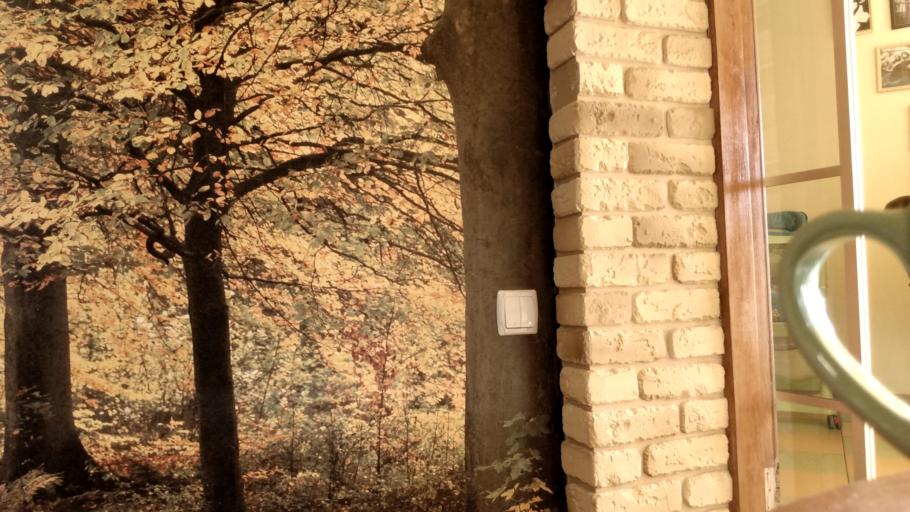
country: RU
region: Vologda
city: Imeni Zhelyabova
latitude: 58.8022
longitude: 36.8905
